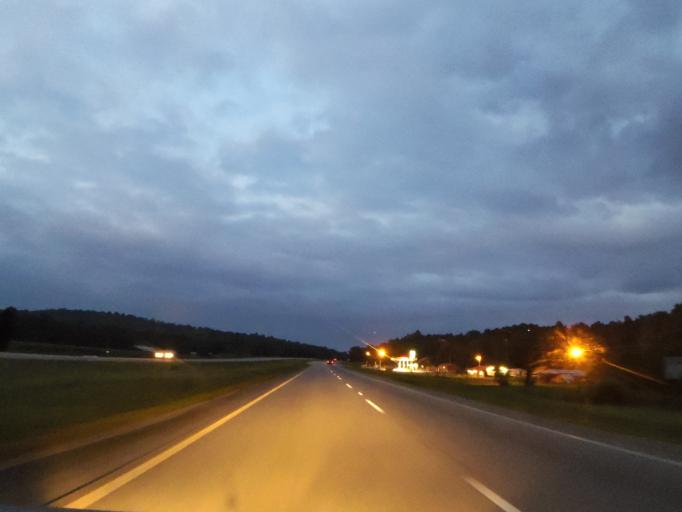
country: US
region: Alabama
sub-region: Madison County
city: New Hope
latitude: 34.6113
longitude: -86.2445
